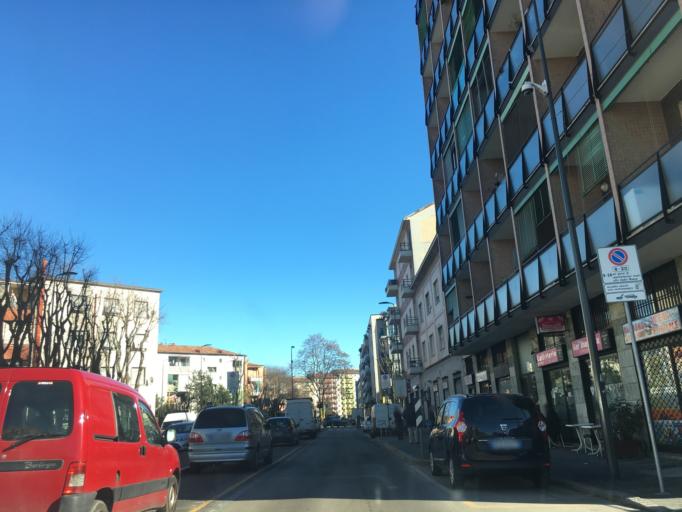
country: IT
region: Lombardy
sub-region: Citta metropolitana di Milano
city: Romano Banco
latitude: 45.4710
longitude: 9.1340
